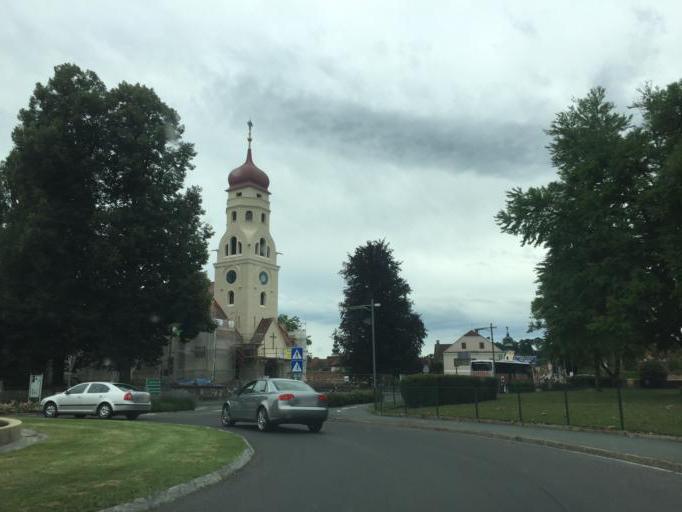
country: AT
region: Styria
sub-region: Politischer Bezirk Suedoststeiermark
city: Bad Radkersburg
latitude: 46.6914
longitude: 15.9878
